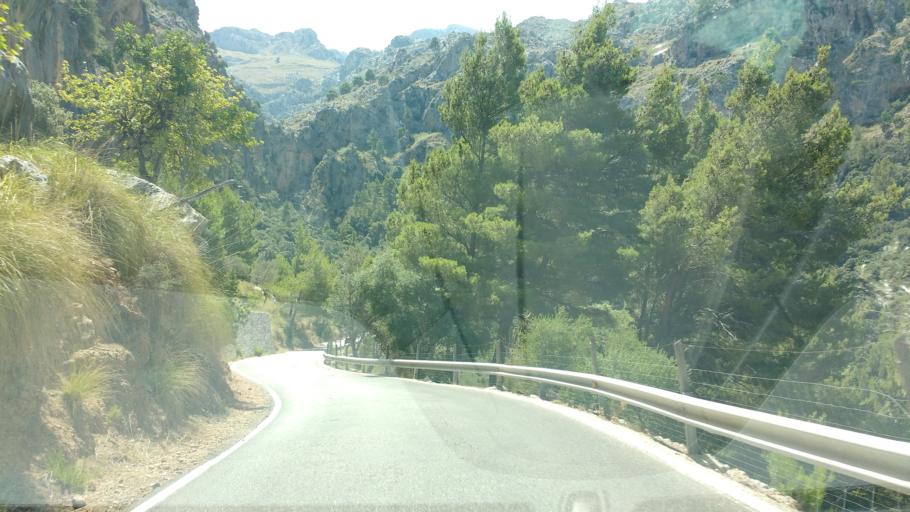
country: ES
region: Balearic Islands
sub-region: Illes Balears
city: Escorca
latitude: 39.8413
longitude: 2.7988
